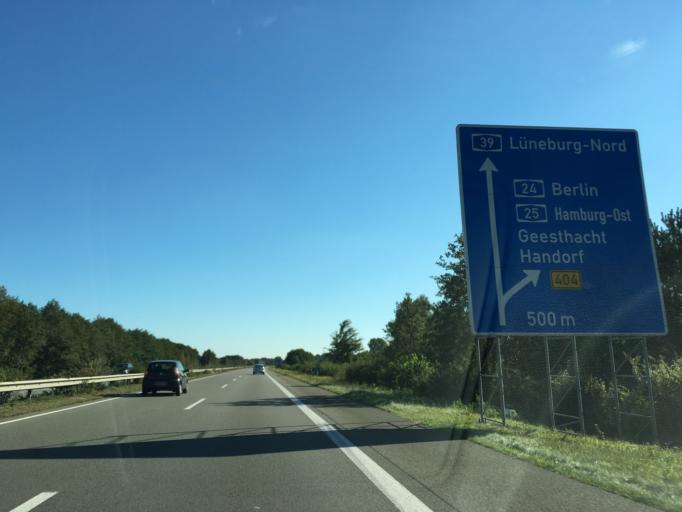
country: DE
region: Lower Saxony
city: Mechtersen
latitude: 53.3140
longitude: 10.3196
